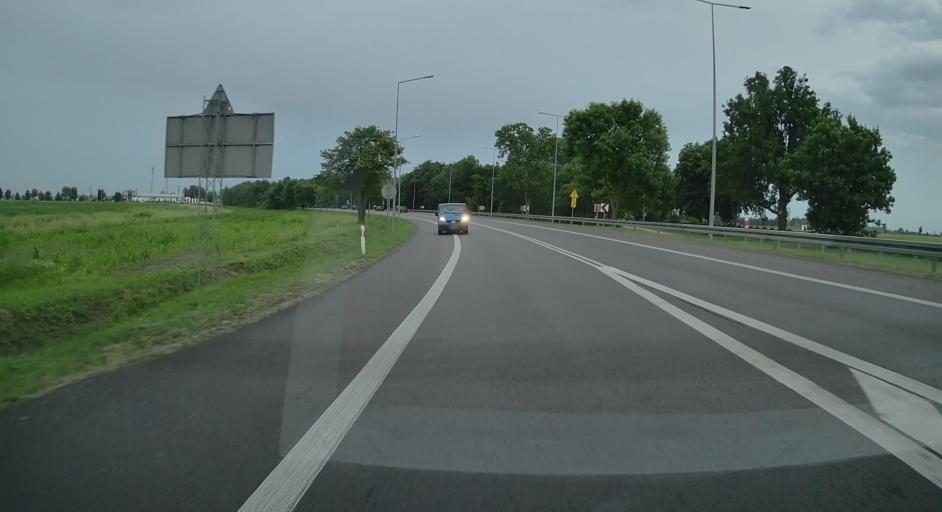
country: PL
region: Lublin Voivodeship
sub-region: Powiat bialski
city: Miedzyrzec Podlaski
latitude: 52.0011
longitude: 22.7572
